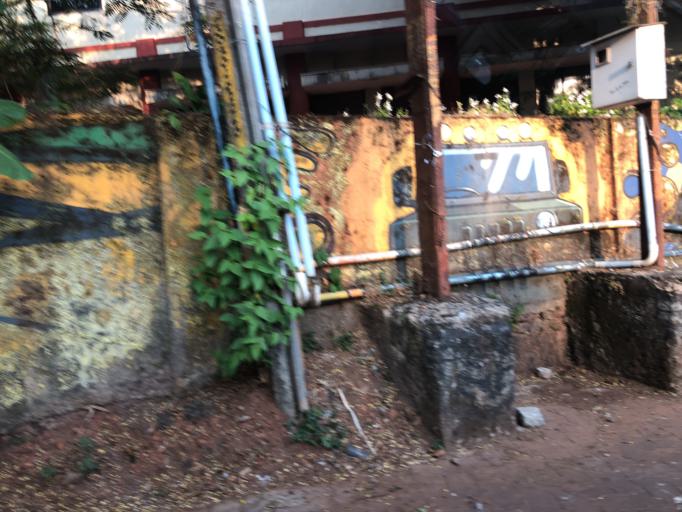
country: IN
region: Karnataka
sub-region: Dakshina Kannada
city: Mangalore
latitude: 12.8718
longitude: 74.8457
